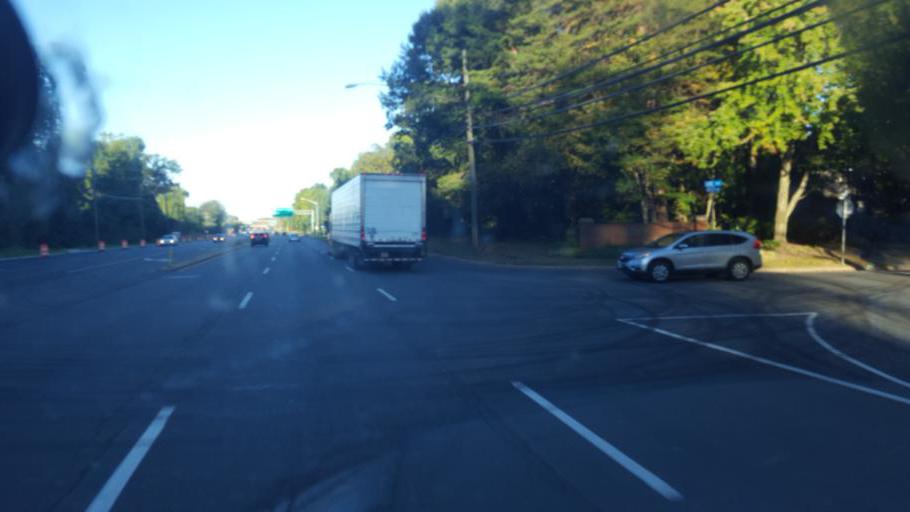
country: US
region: Virginia
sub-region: Fairfax County
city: Greenbriar
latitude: 38.8483
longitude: -77.3589
